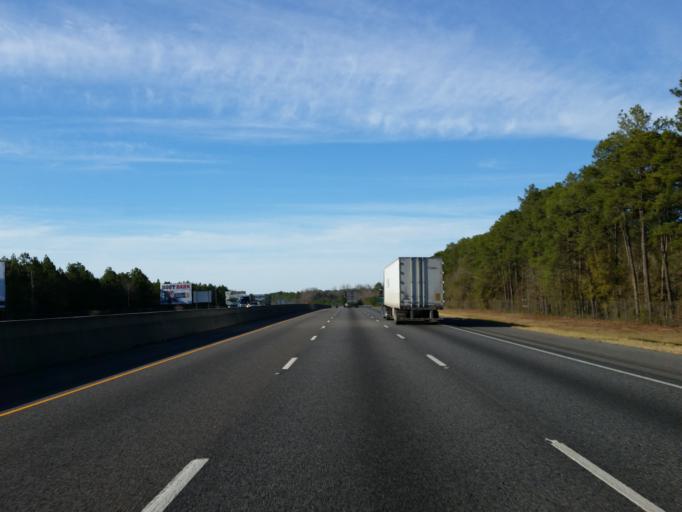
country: US
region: Georgia
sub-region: Lowndes County
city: Remerton
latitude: 30.8665
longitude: -83.3383
